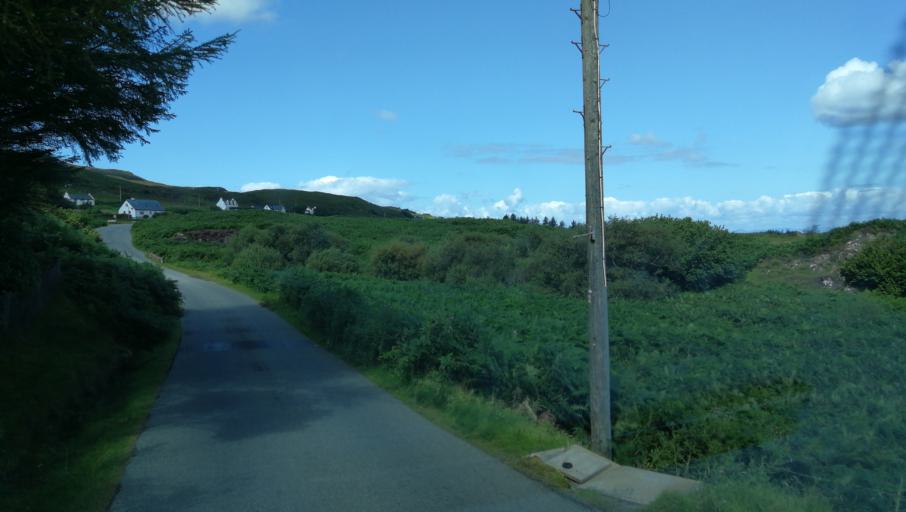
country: GB
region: Scotland
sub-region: Highland
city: Isle of Skye
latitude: 57.4382
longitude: -6.6340
